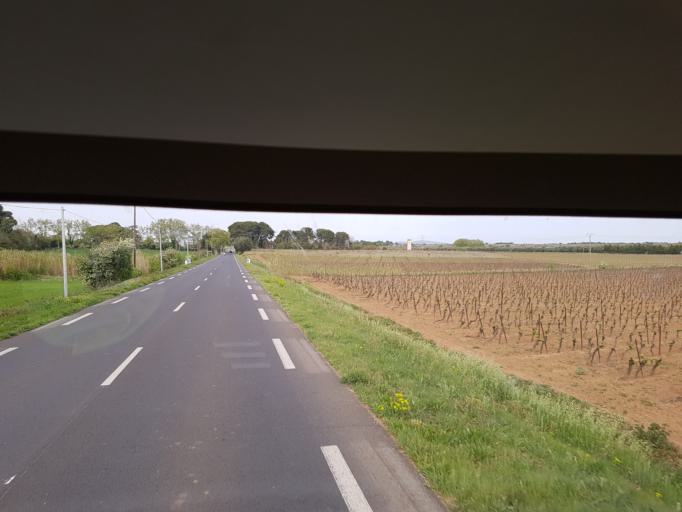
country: FR
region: Languedoc-Roussillon
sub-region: Departement de l'Herault
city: Agde
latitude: 43.3379
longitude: 3.4951
